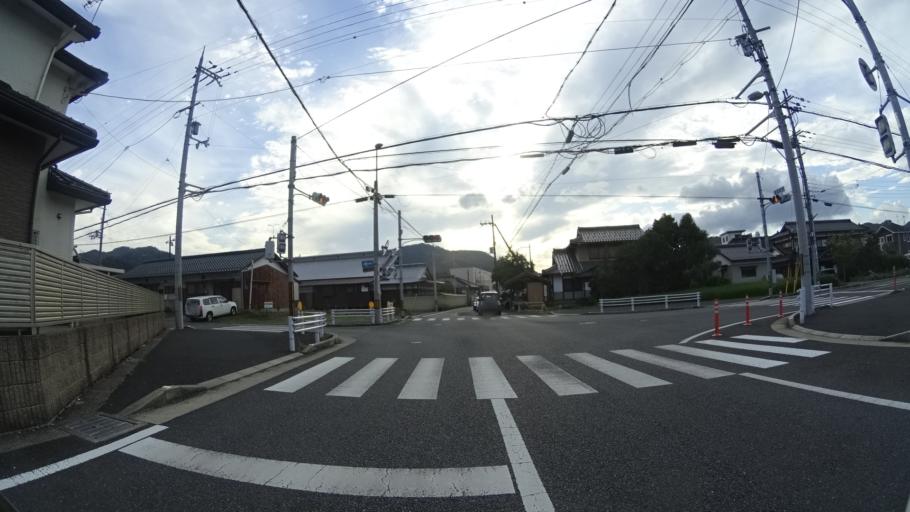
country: JP
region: Kyoto
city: Maizuru
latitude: 35.4267
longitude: 135.3325
